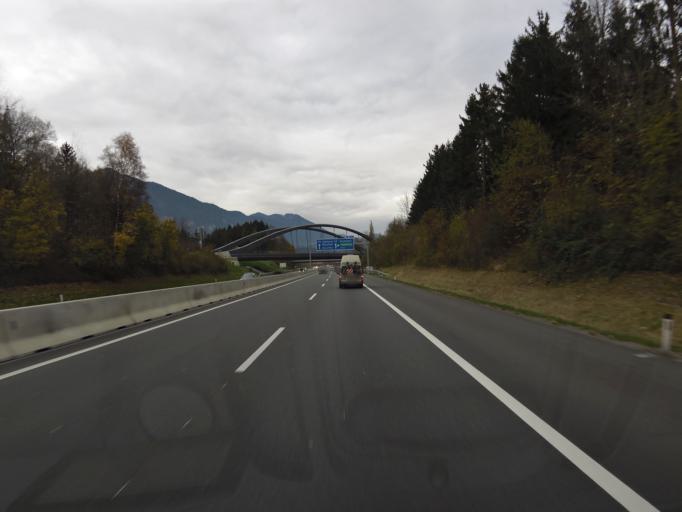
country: AT
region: Tyrol
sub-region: Politischer Bezirk Kufstein
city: Brixlegg
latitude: 47.4318
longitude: 11.8701
